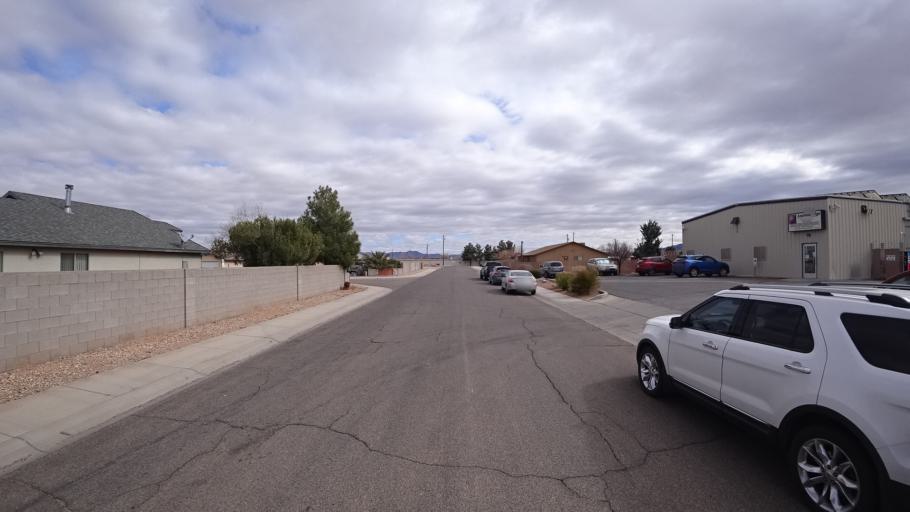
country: US
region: Arizona
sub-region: Mohave County
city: New Kingman-Butler
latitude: 35.2322
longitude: -114.0011
